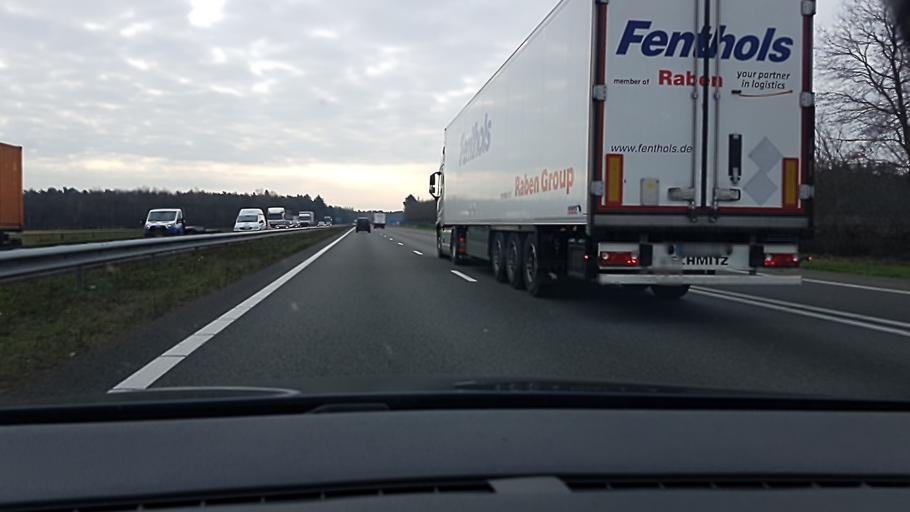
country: NL
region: North Brabant
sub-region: Gemeente Boxmeer
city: Overloon
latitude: 51.5809
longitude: 5.9837
